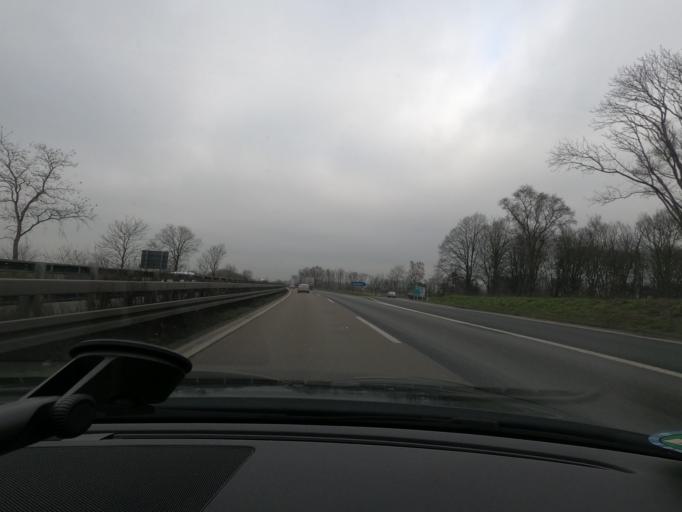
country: DE
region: North Rhine-Westphalia
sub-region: Regierungsbezirk Dusseldorf
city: Monchengladbach
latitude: 51.1404
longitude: 6.4226
